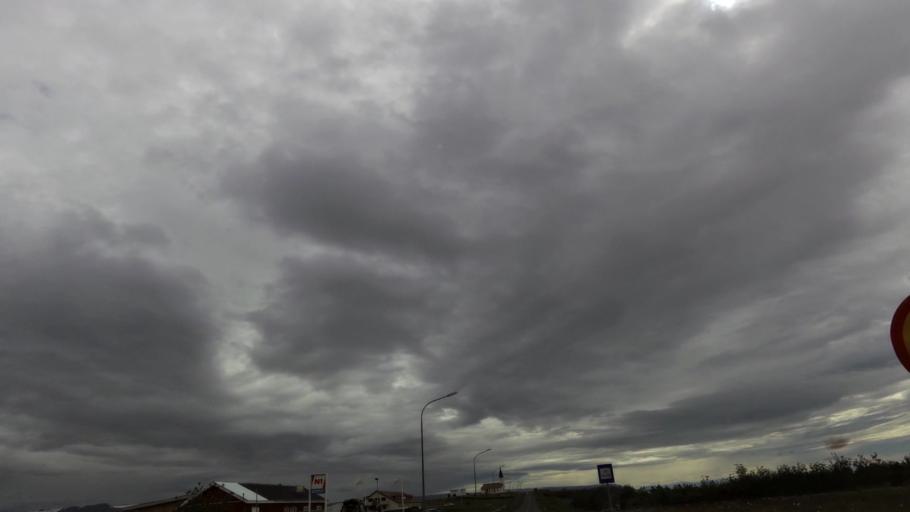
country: IS
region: West
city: Stykkisholmur
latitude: 65.4521
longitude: -22.2019
